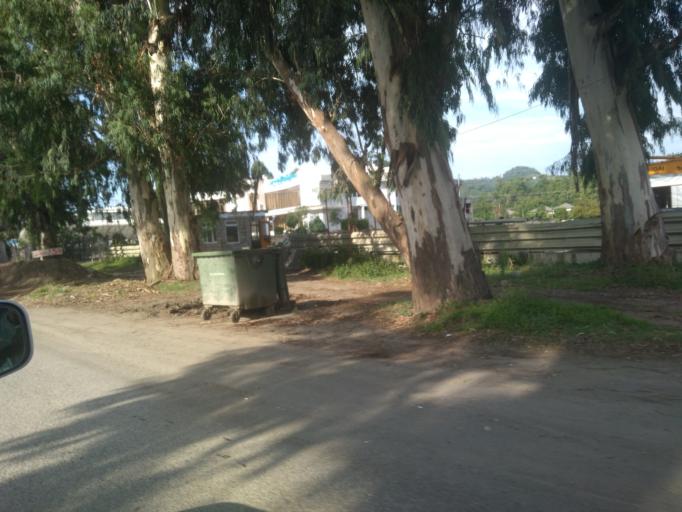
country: GE
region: Ajaria
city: Khelvachauri
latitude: 41.5930
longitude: 41.6440
